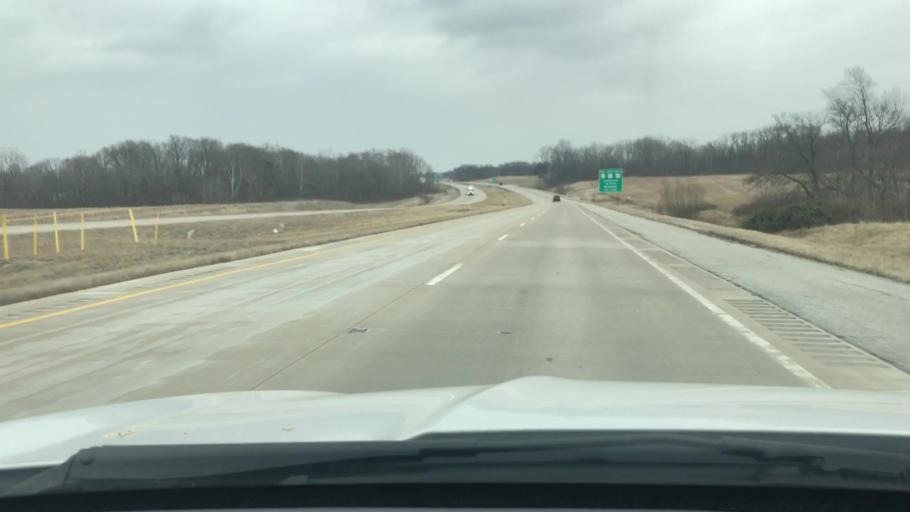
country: US
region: Indiana
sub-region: Cass County
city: Dunkirk
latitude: 40.7275
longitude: -86.4042
